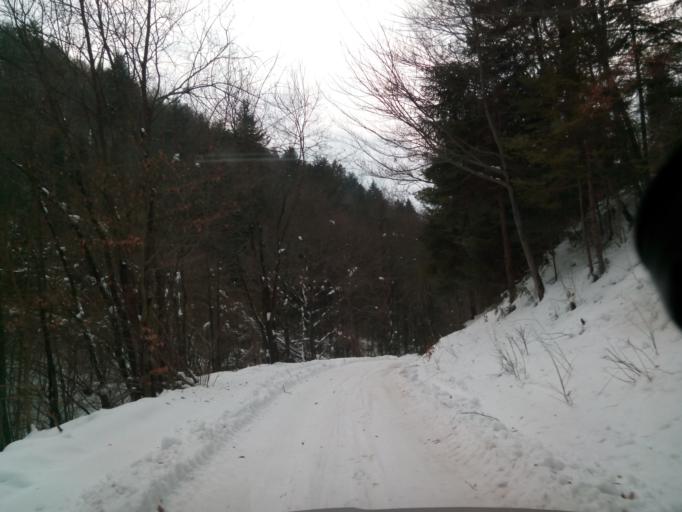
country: SK
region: Presovsky
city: Sabinov
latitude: 49.2096
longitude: 21.0940
